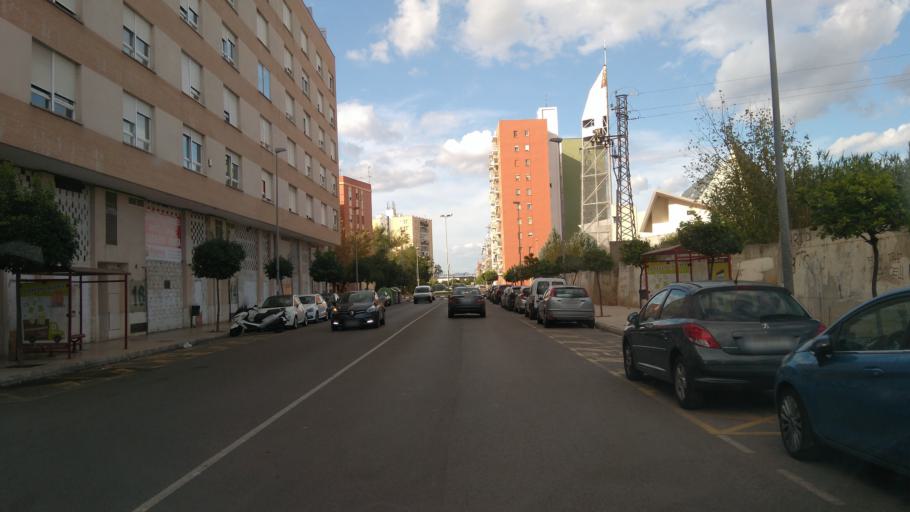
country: ES
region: Valencia
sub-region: Provincia de Valencia
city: Alzira
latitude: 39.1559
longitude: -0.4277
